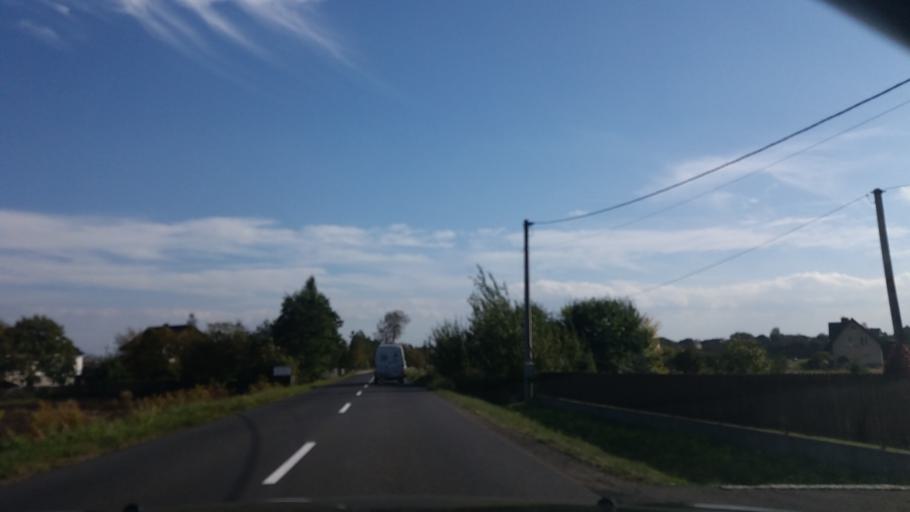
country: PL
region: Lesser Poland Voivodeship
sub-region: Powiat chrzanowski
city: Grojec
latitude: 50.0953
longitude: 19.5549
